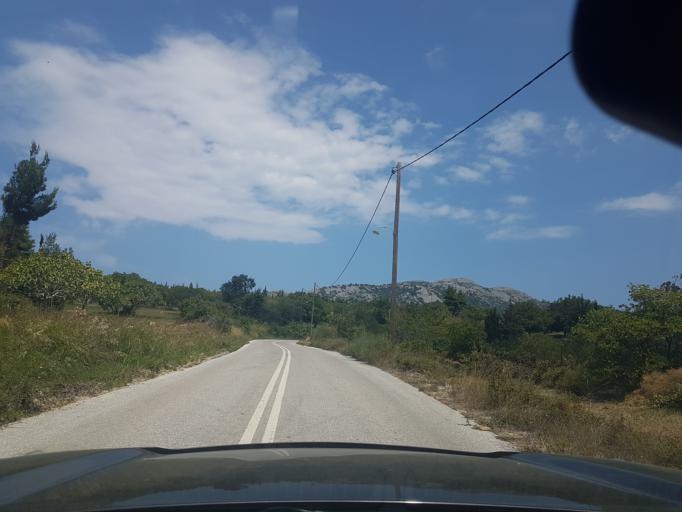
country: GR
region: Central Greece
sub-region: Nomos Evvoias
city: Kymi
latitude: 38.6465
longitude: 24.0393
